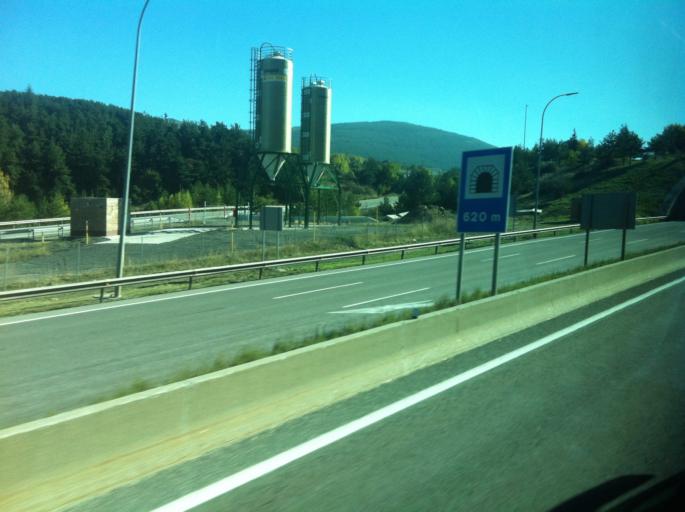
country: ES
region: Madrid
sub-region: Provincia de Madrid
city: Somosierra
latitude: 41.1377
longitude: -3.5821
